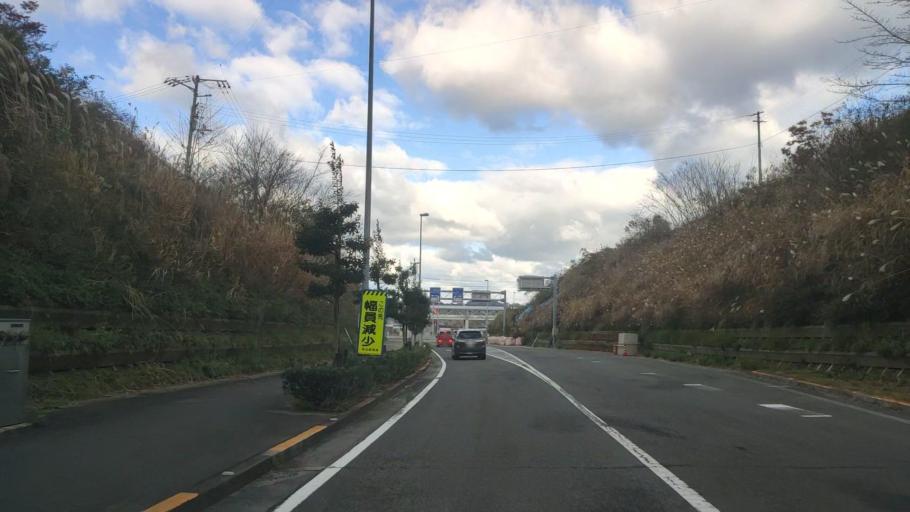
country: JP
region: Ehime
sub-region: Shikoku-chuo Shi
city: Matsuyama
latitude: 33.8878
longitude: 132.7066
